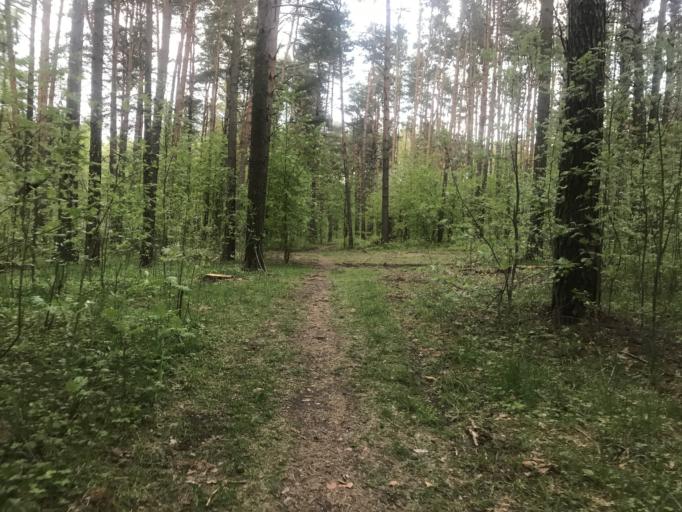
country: BY
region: Minsk
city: Zhdanovichy
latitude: 53.9531
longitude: 27.4231
